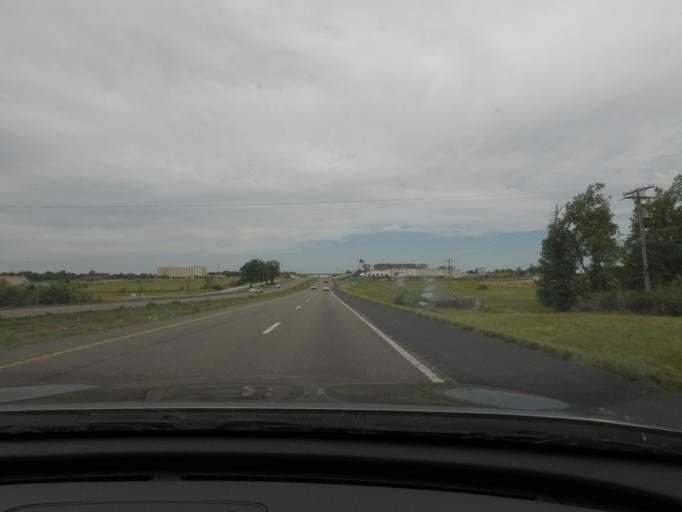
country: US
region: Missouri
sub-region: Boone County
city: Columbia
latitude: 38.9602
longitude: -92.2459
